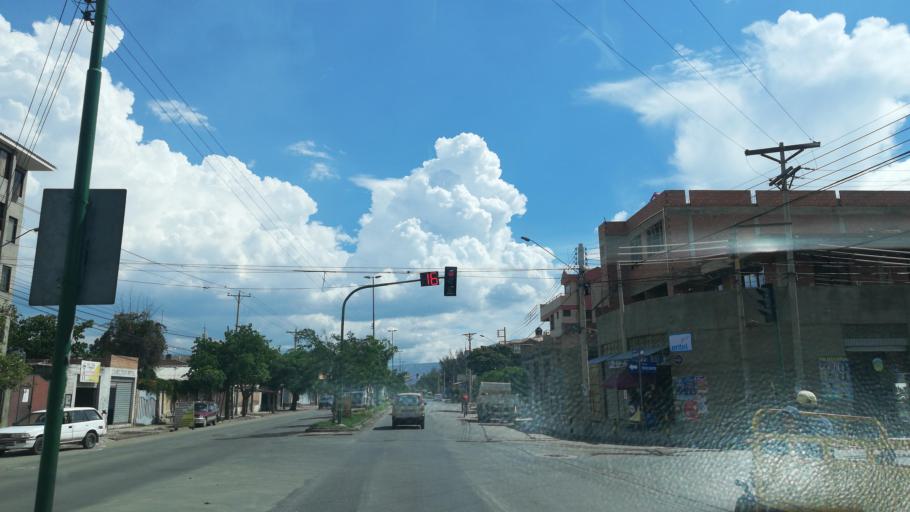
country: BO
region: Cochabamba
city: Cochabamba
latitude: -17.4185
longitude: -66.1663
